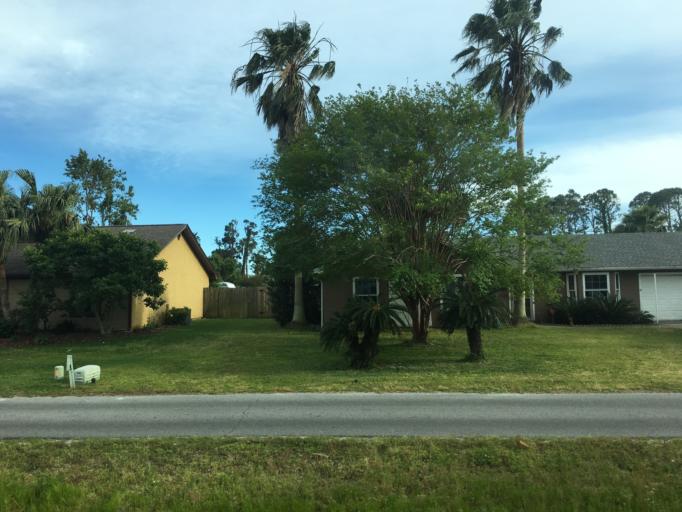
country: US
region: Florida
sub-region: Bay County
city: Panama City Beach
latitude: 30.1756
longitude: -85.7744
